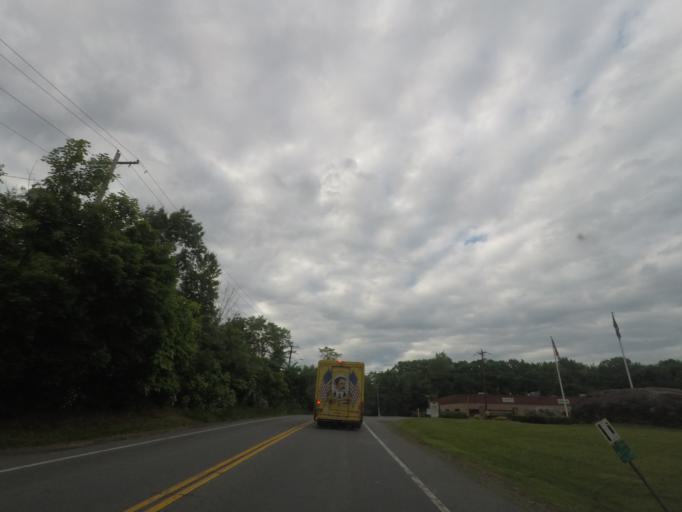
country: US
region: New York
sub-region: Orange County
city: Gardnertown
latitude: 41.5424
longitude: -74.0618
